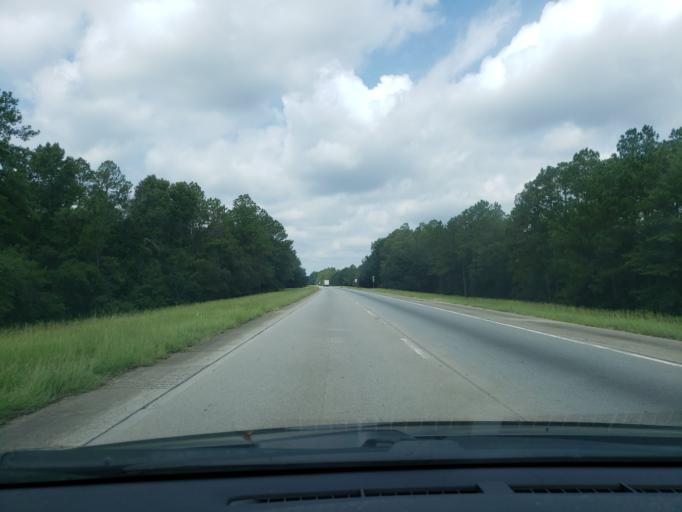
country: US
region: Georgia
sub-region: Treutlen County
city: Soperton
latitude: 32.4228
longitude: -82.4201
